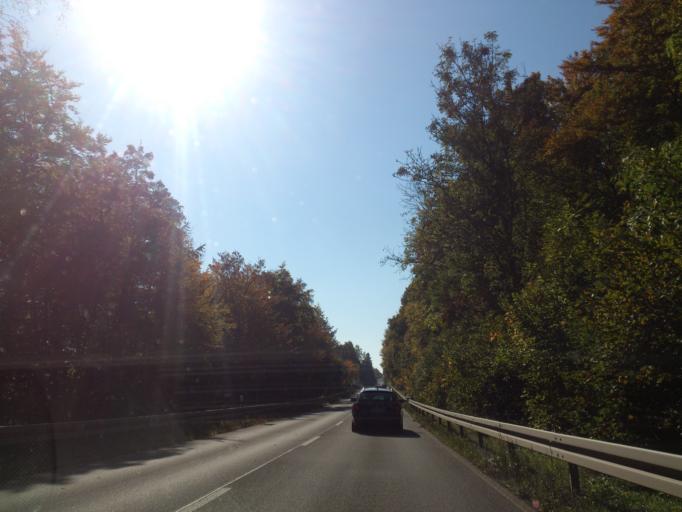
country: DE
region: Hesse
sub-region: Regierungsbezirk Kassel
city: Vellmar
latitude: 51.3453
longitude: 9.4157
